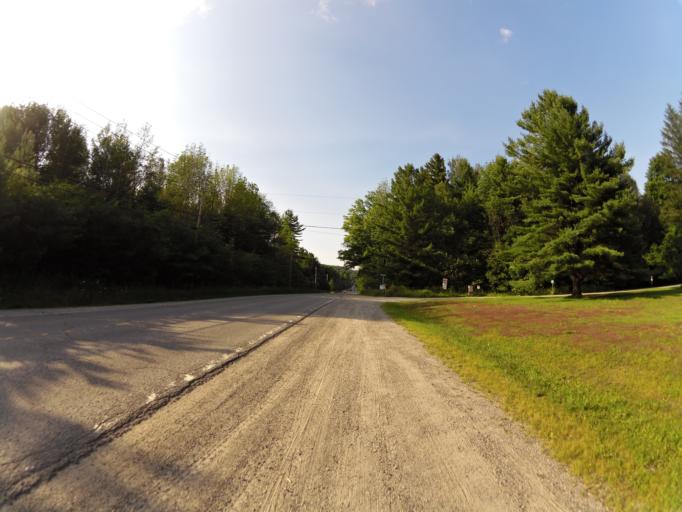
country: CA
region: Quebec
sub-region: Outaouais
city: Gatineau
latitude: 45.4902
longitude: -75.8132
